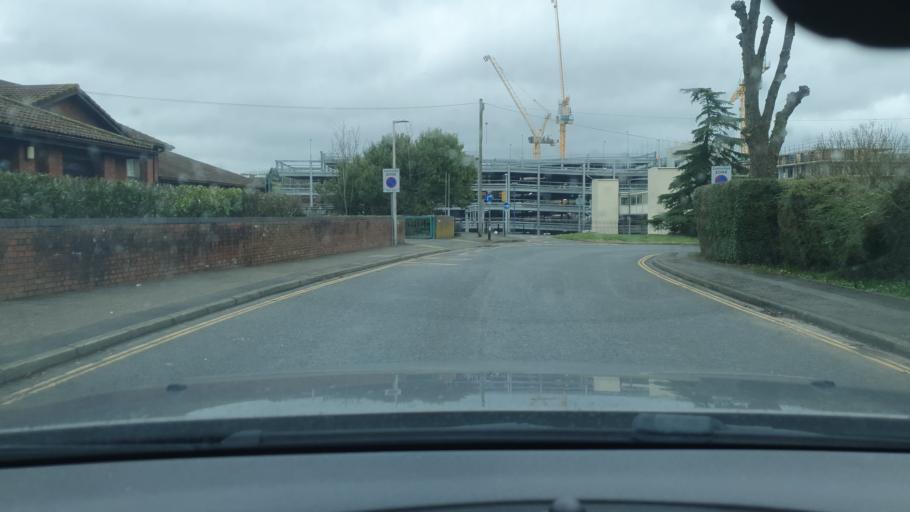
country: GB
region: England
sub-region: West Berkshire
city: Newbury
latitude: 51.3964
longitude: -1.3244
